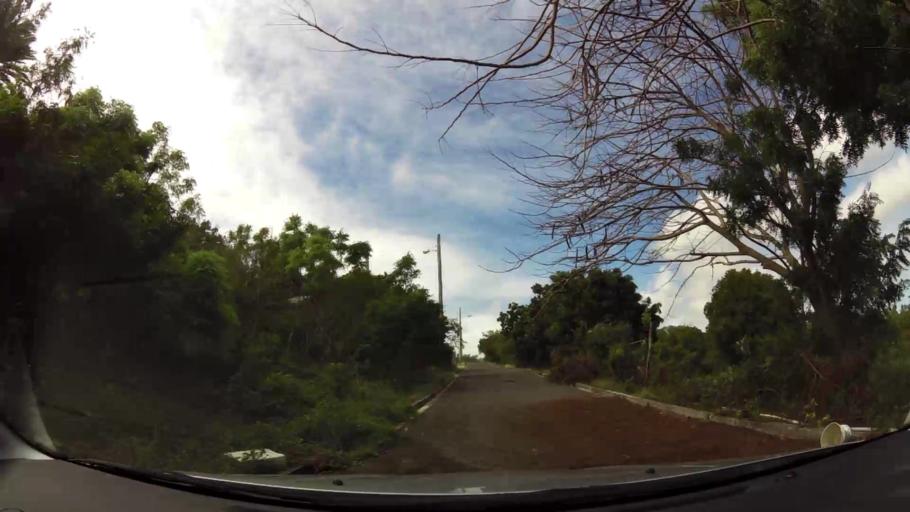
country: AG
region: Saint Paul
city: Falmouth
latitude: 17.0465
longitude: -61.7250
